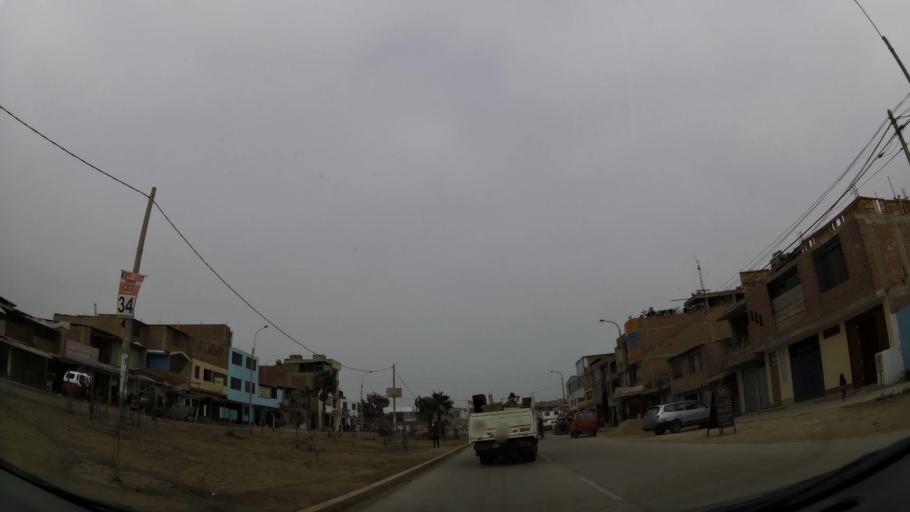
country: PE
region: Lima
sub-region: Lima
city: Surco
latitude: -12.2274
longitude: -76.9455
